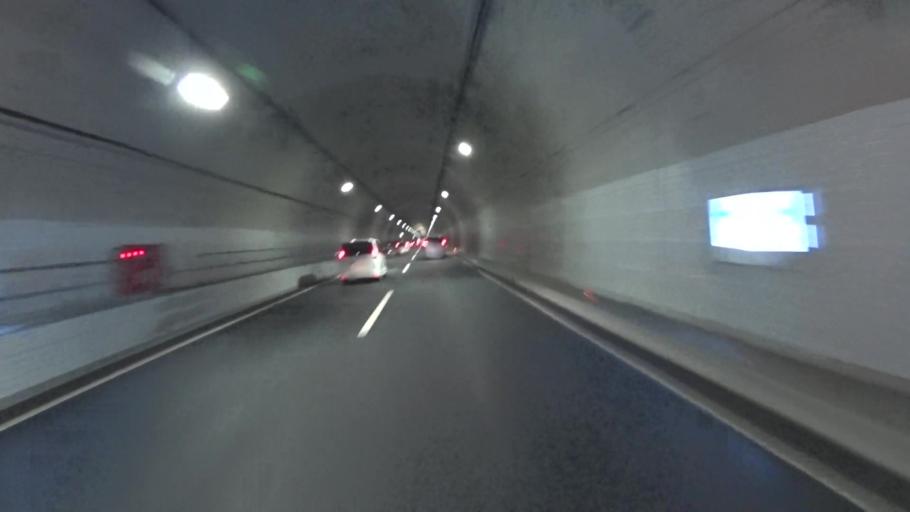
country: JP
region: Kyoto
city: Muko
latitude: 34.9358
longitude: 135.6651
